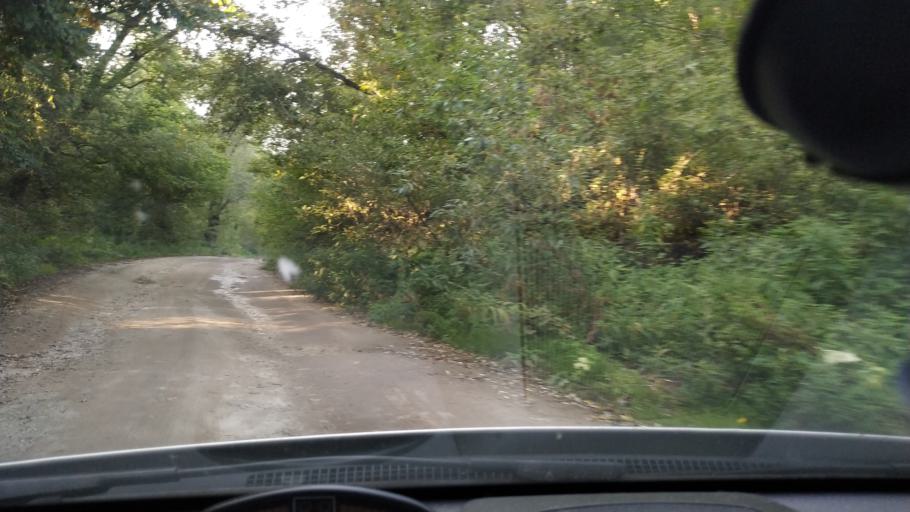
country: RU
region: Rjazan
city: Rybnoye
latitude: 54.8685
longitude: 39.6532
